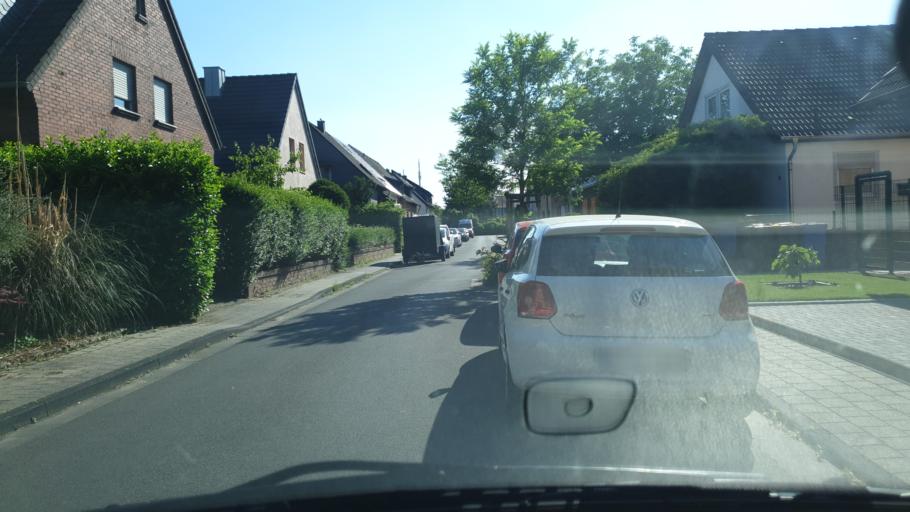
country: DE
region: North Rhine-Westphalia
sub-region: Regierungsbezirk Koln
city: Kerpen
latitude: 50.8991
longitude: 6.6716
